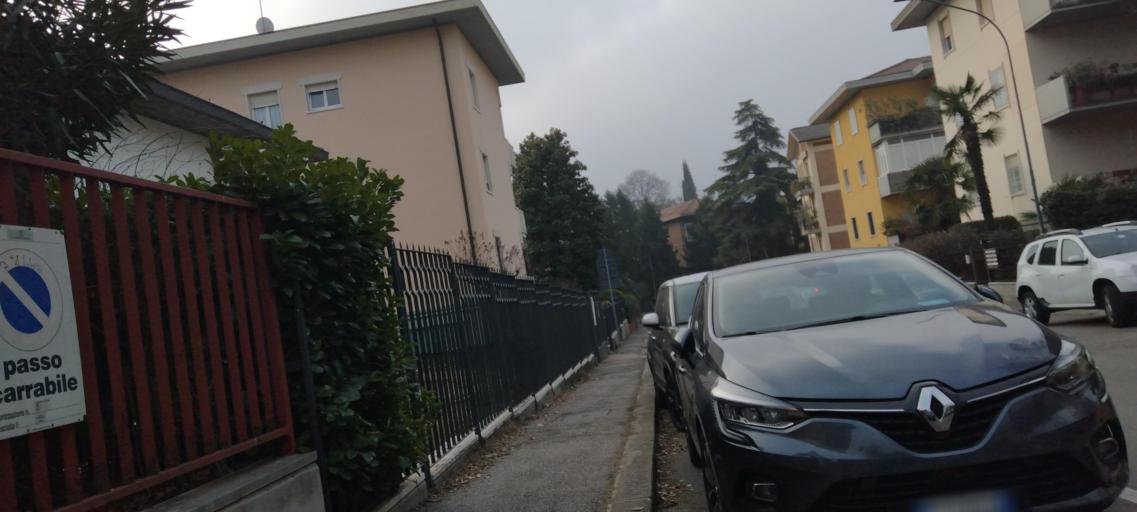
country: IT
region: Veneto
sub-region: Provincia di Verona
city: Verona
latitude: 45.4591
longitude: 10.9862
